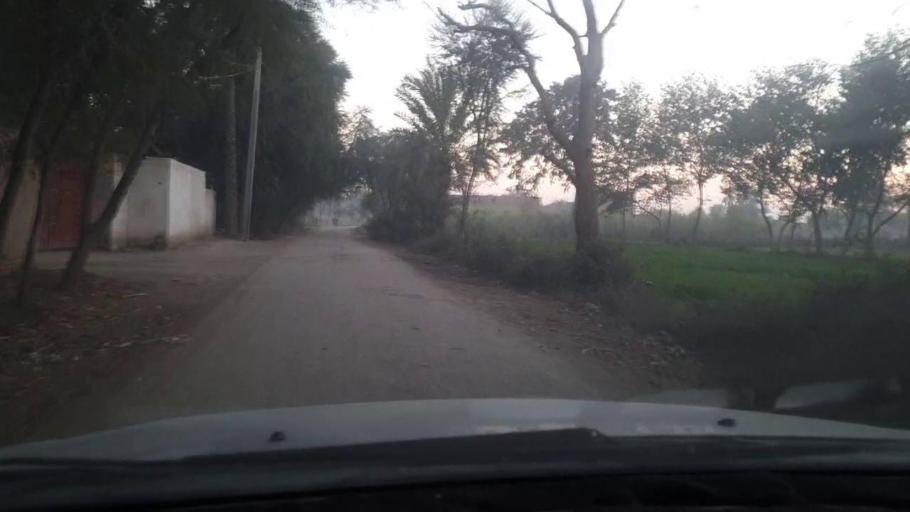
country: PK
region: Sindh
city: Ghotki
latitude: 28.0057
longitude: 69.3378
